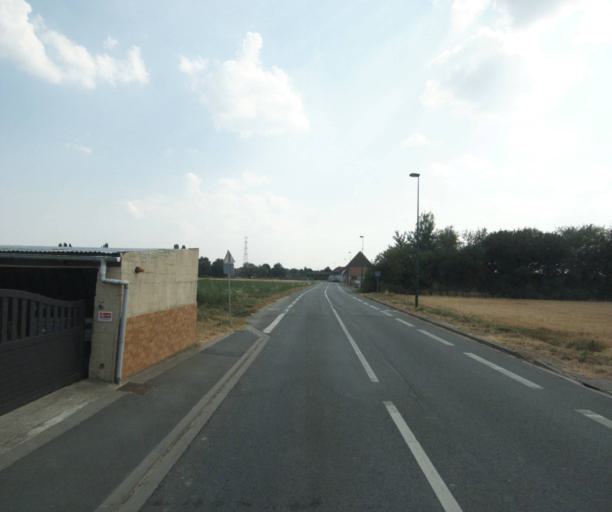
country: FR
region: Nord-Pas-de-Calais
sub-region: Departement du Nord
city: Linselles
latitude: 50.7242
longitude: 3.0808
